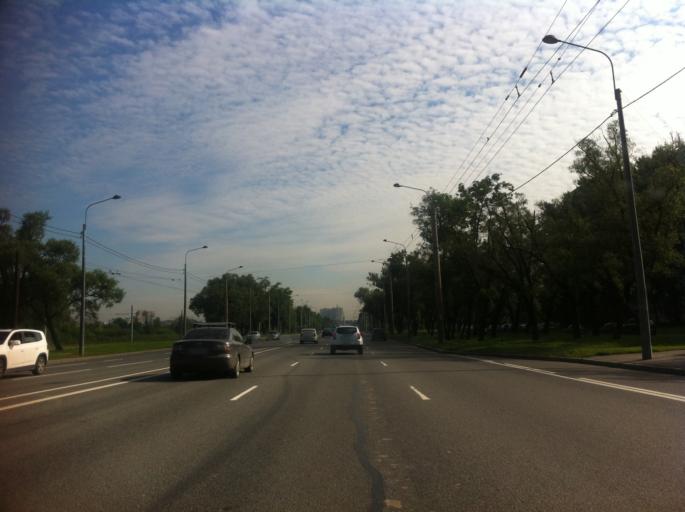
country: RU
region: St.-Petersburg
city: Uritsk
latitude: 59.8368
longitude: 30.2000
